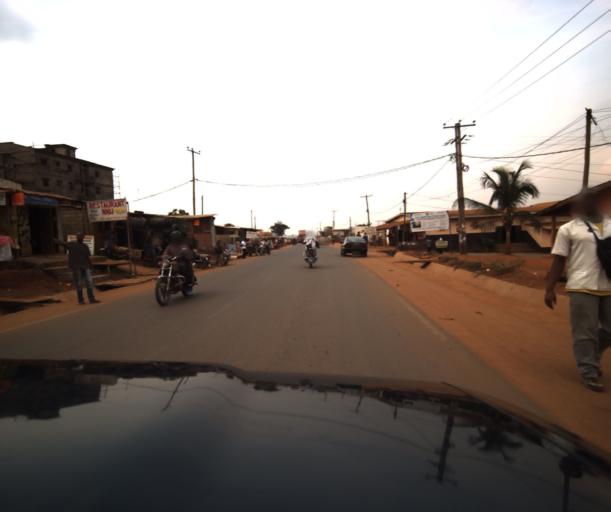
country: CM
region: Centre
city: Yaounde
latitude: 3.8374
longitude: 11.4746
